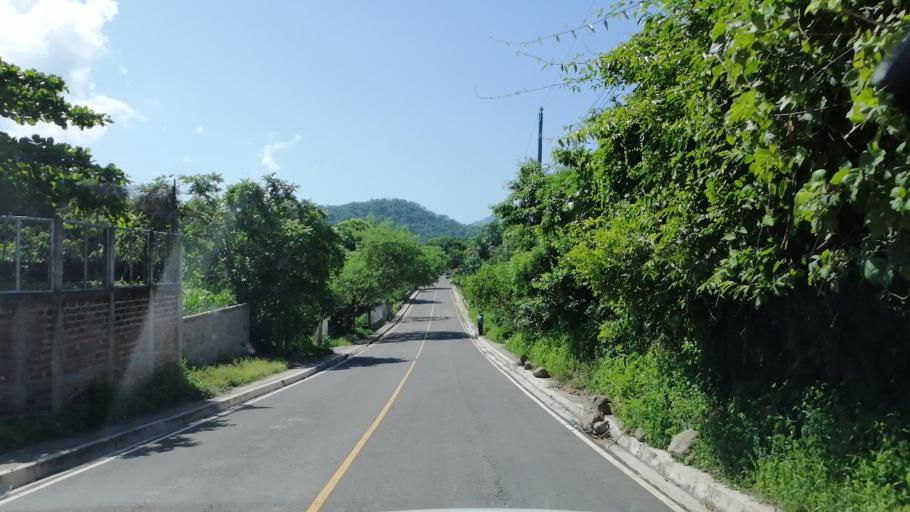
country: SV
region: Cabanas
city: Victoria
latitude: 13.9513
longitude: -88.7314
